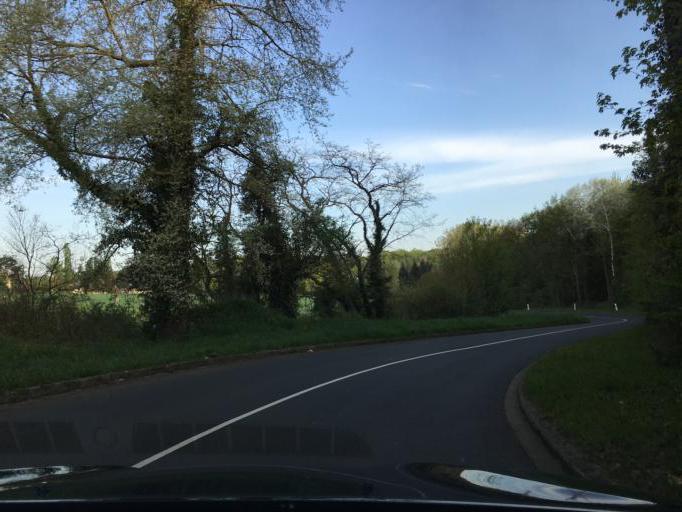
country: FR
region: Ile-de-France
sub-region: Departement des Yvelines
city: Gazeran
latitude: 48.5775
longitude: 1.7908
